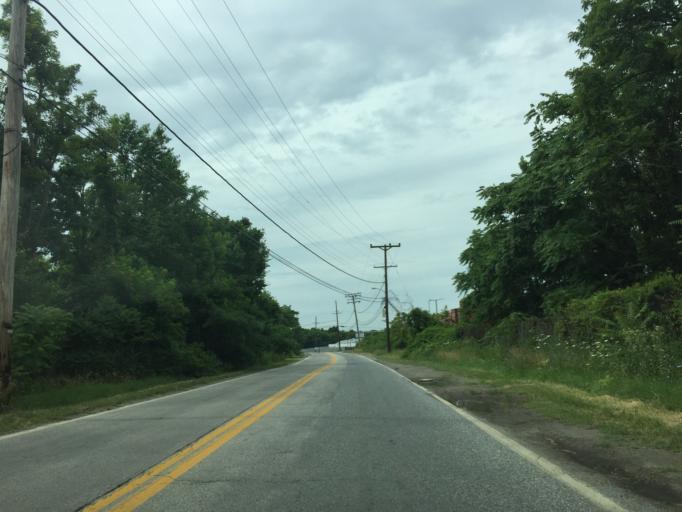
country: US
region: Maryland
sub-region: Baltimore County
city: Edgemere
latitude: 39.2731
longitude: -76.4613
